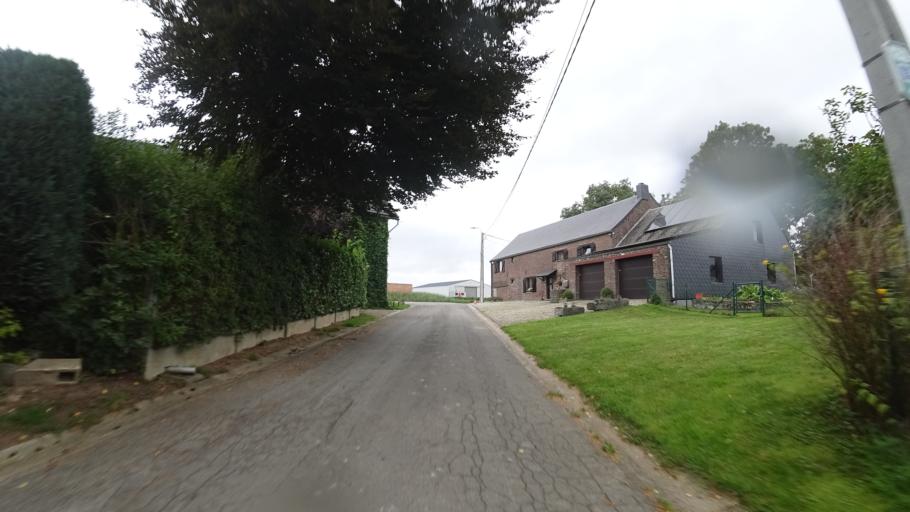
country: BE
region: Wallonia
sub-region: Province de Namur
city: Namur
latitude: 50.5409
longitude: 4.8335
